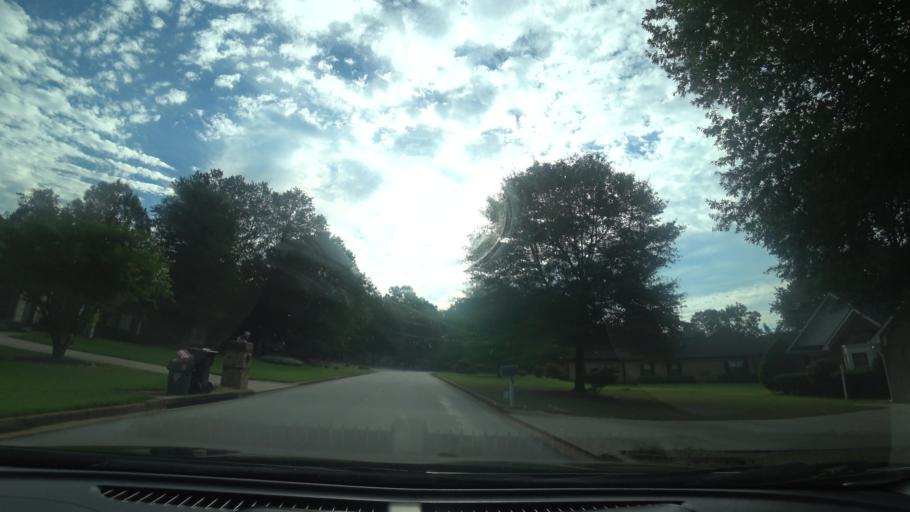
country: US
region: Georgia
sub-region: Newton County
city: Porterdale
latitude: 33.6136
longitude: -83.9495
